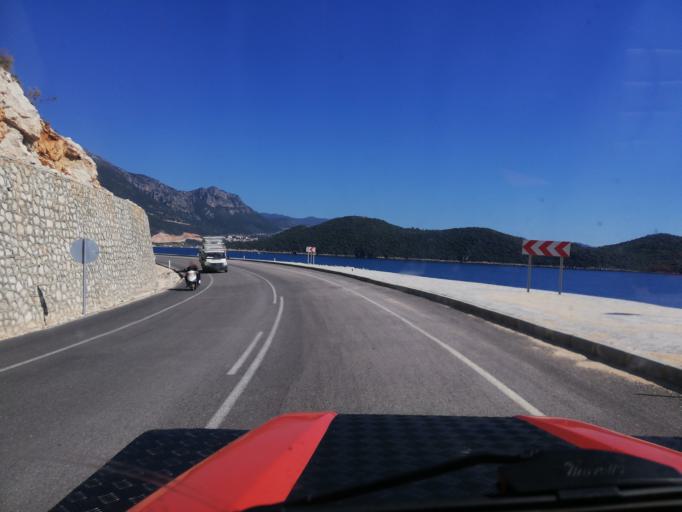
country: TR
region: Antalya
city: Kas
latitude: 36.2028
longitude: 29.5949
